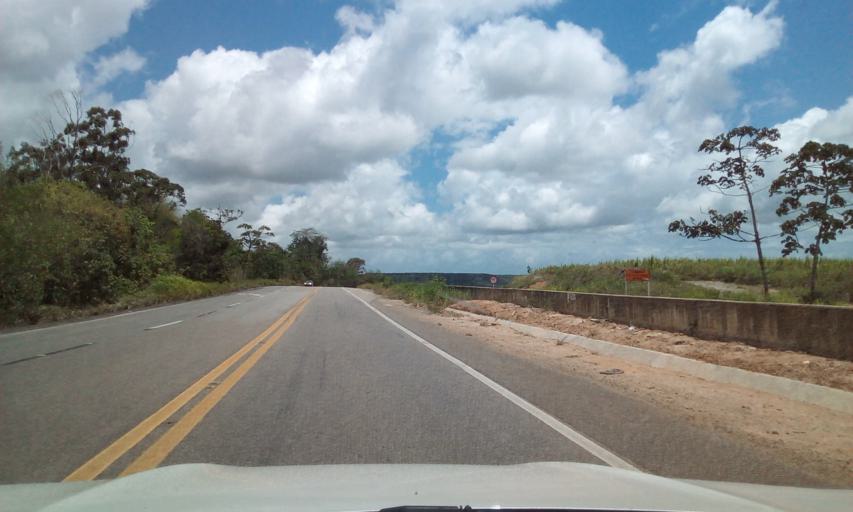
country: BR
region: Alagoas
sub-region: Sao Miguel Dos Campos
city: Sao Miguel dos Campos
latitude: -9.8901
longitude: -36.1576
